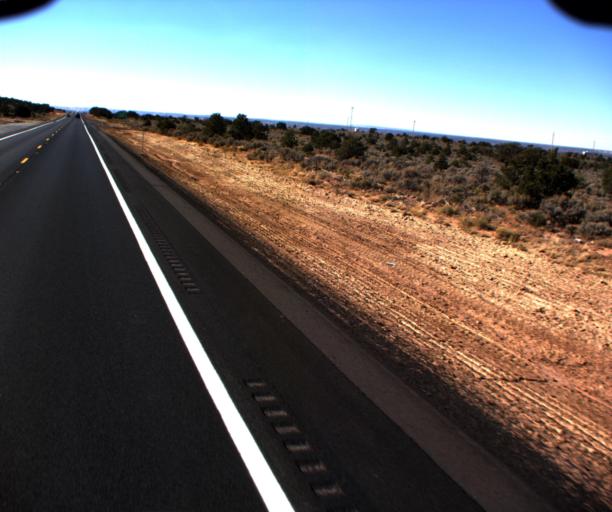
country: US
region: Arizona
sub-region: Apache County
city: Ganado
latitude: 35.7174
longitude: -109.4065
